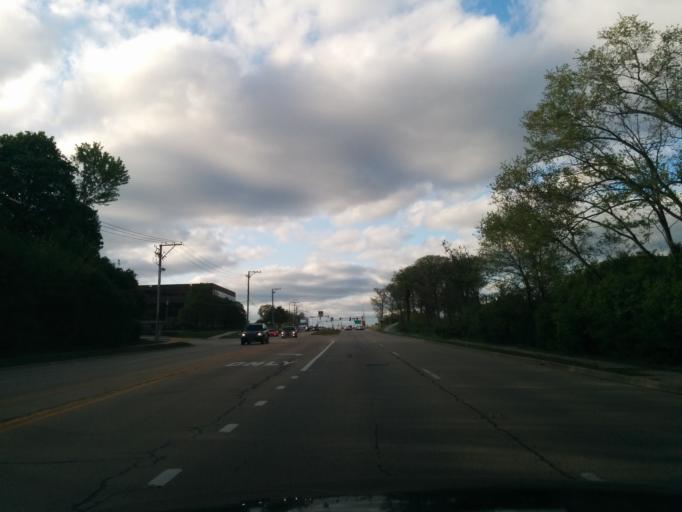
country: US
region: Illinois
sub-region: DuPage County
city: Downers Grove
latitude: 41.8283
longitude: -88.0107
